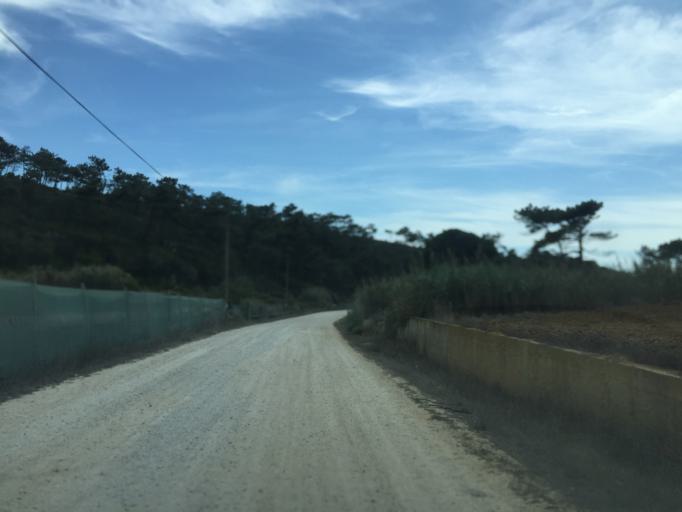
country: PT
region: Lisbon
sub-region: Torres Vedras
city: A dos Cunhados
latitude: 39.1848
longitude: -9.3402
